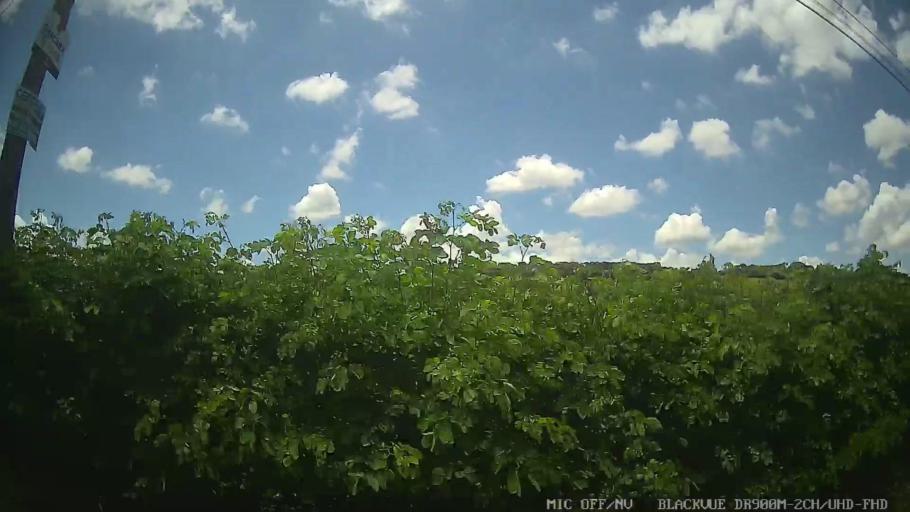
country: BR
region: Sao Paulo
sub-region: Atibaia
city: Atibaia
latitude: -23.0490
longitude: -46.5037
